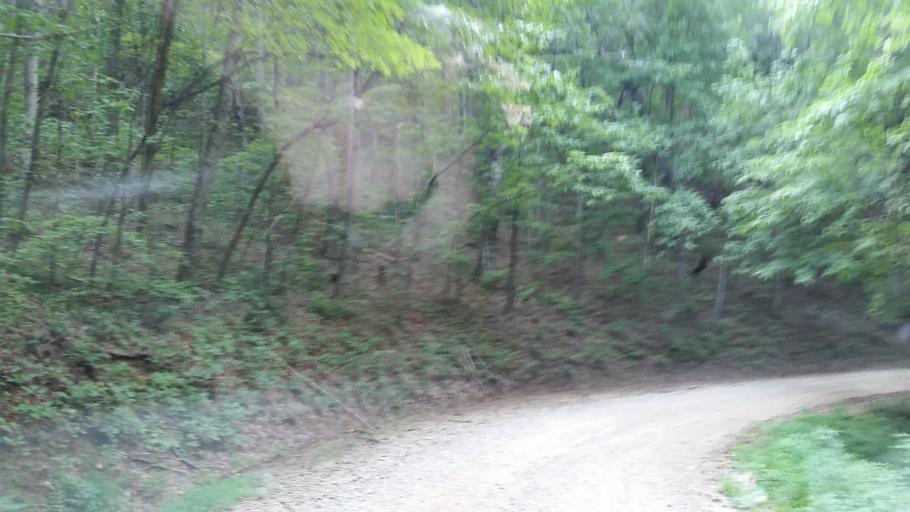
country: US
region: Georgia
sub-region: Lumpkin County
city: Dahlonega
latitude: 34.6431
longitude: -84.0479
